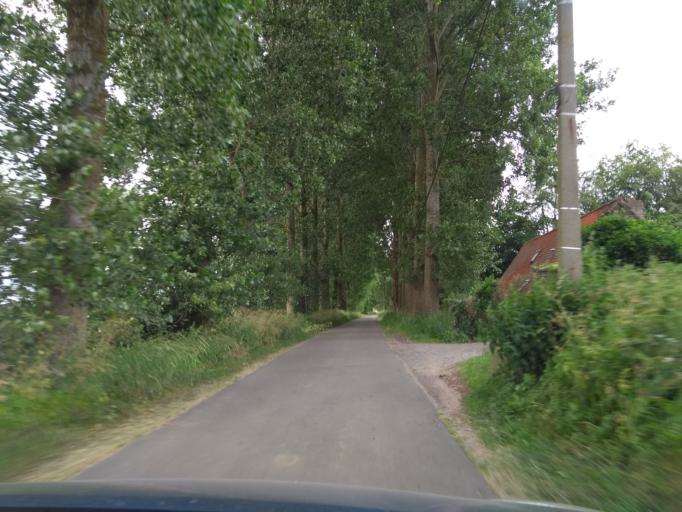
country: BE
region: Flanders
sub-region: Provincie Oost-Vlaanderen
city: Nevele
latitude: 51.0732
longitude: 3.5175
